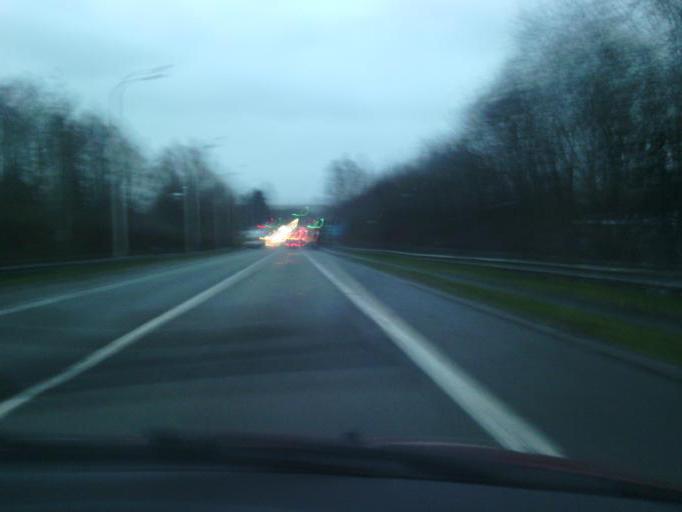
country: BE
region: Flanders
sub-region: Provincie Oost-Vlaanderen
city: Lokeren
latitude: 51.1016
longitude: 3.9721
